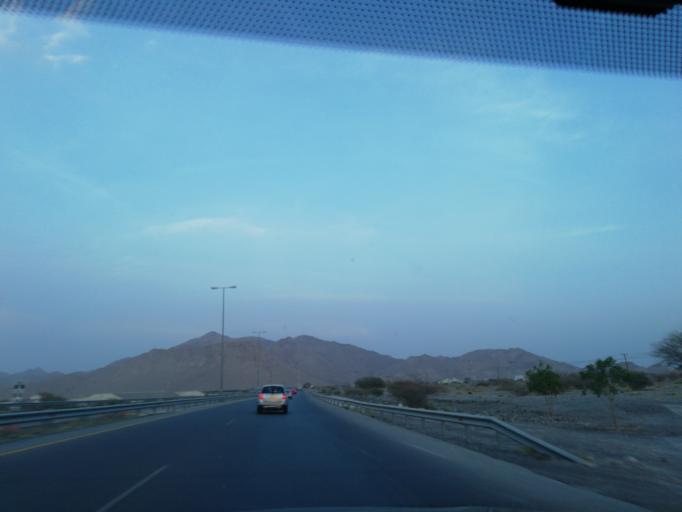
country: OM
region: Muhafazat ad Dakhiliyah
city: Nizwa
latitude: 22.8625
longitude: 57.5834
